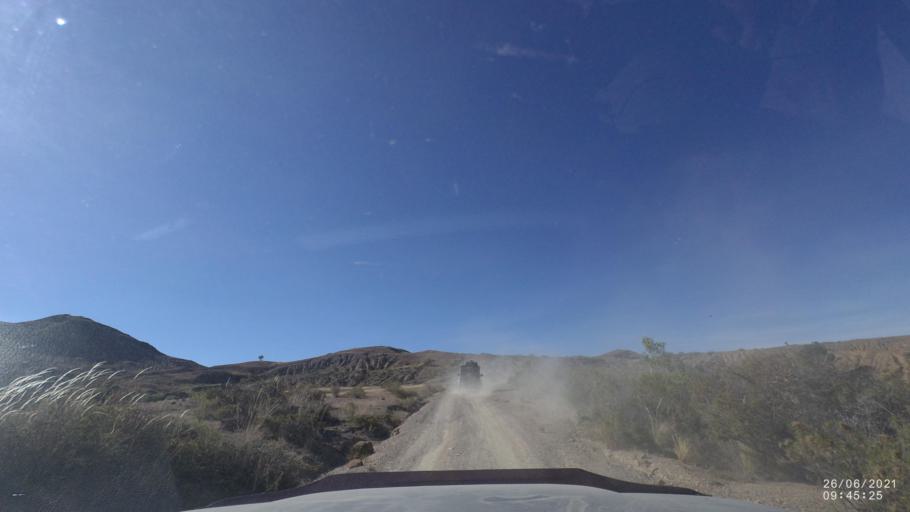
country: BO
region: Cochabamba
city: Mizque
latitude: -17.9476
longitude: -65.6302
